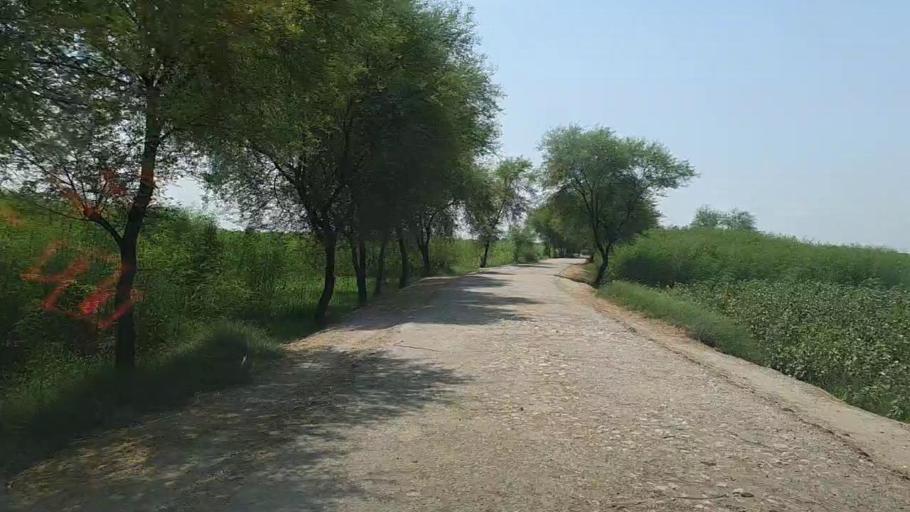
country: PK
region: Sindh
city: Ubauro
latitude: 28.2017
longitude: 69.8025
